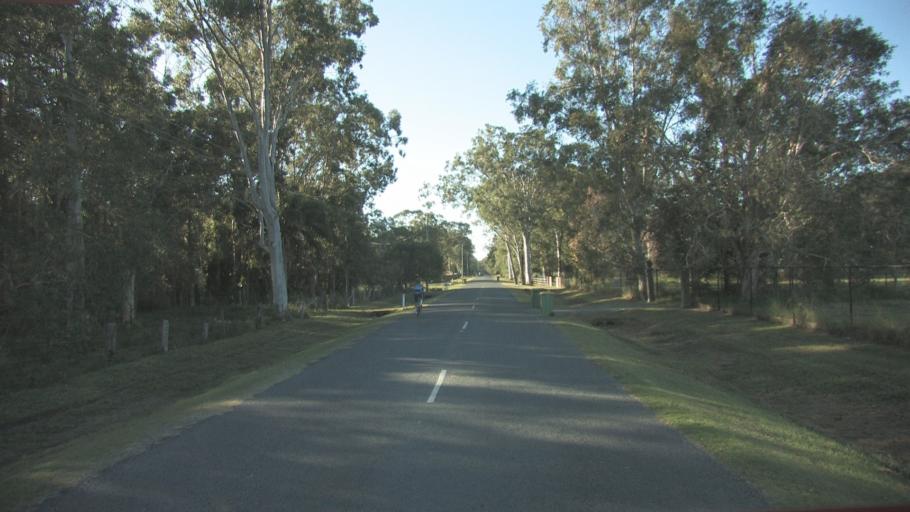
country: AU
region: Queensland
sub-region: Gold Coast
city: Yatala
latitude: -27.6745
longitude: 153.2433
